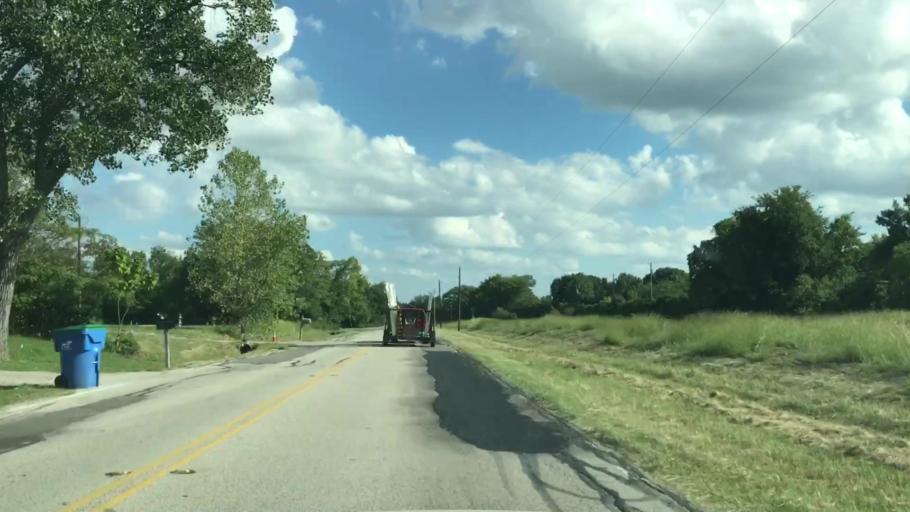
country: US
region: Texas
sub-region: Dallas County
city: Rowlett
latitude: 32.8858
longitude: -96.5293
